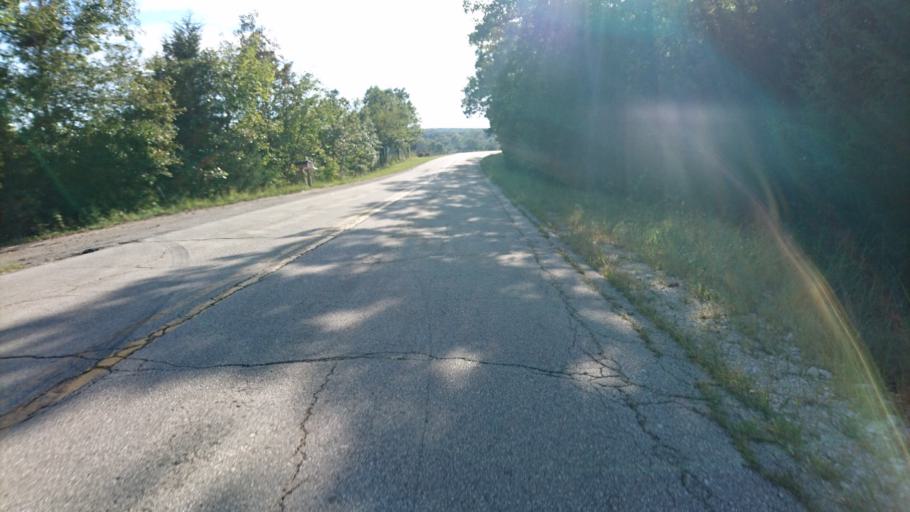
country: US
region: Missouri
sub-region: Crawford County
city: Cuba
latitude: 38.1104
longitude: -91.3325
